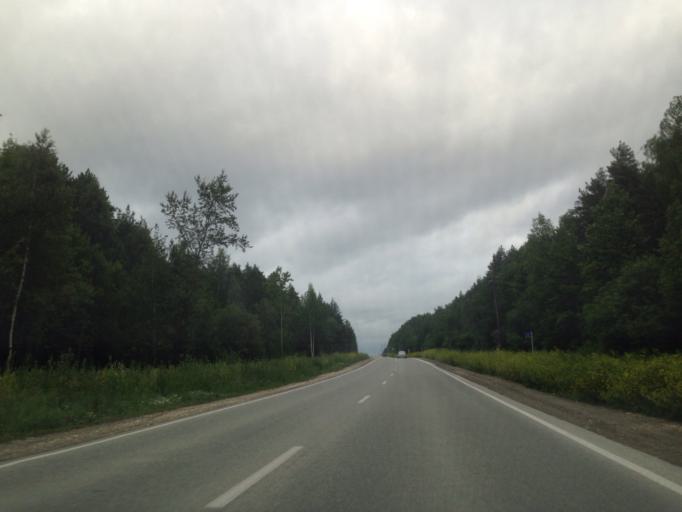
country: RU
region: Sverdlovsk
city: Istok
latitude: 56.8395
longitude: 60.7656
